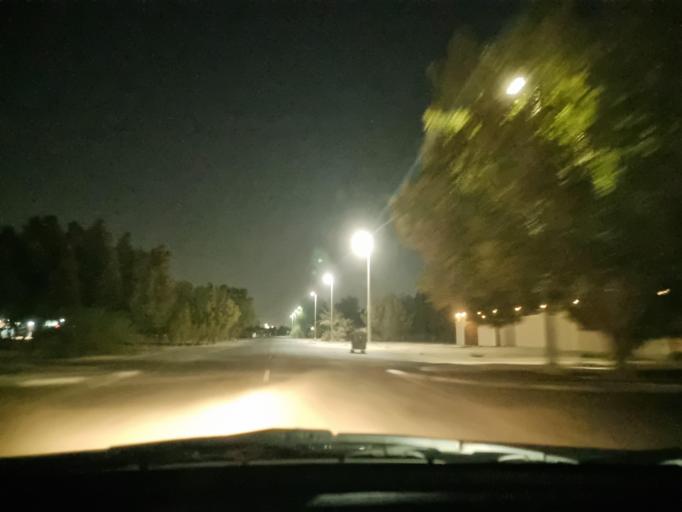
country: AE
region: Abu Dhabi
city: Abu Dhabi
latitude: 24.3825
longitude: 54.6971
